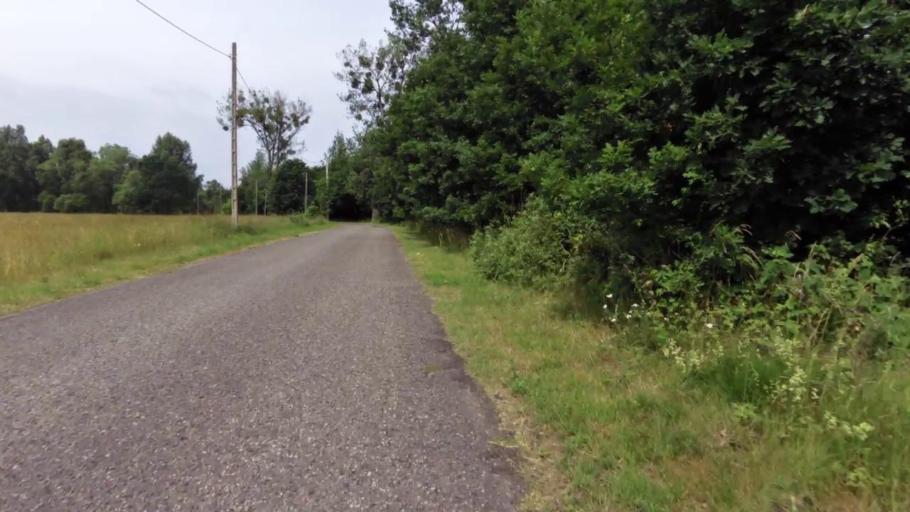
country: PL
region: West Pomeranian Voivodeship
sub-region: Powiat kamienski
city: Wolin
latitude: 53.7640
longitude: 14.6568
